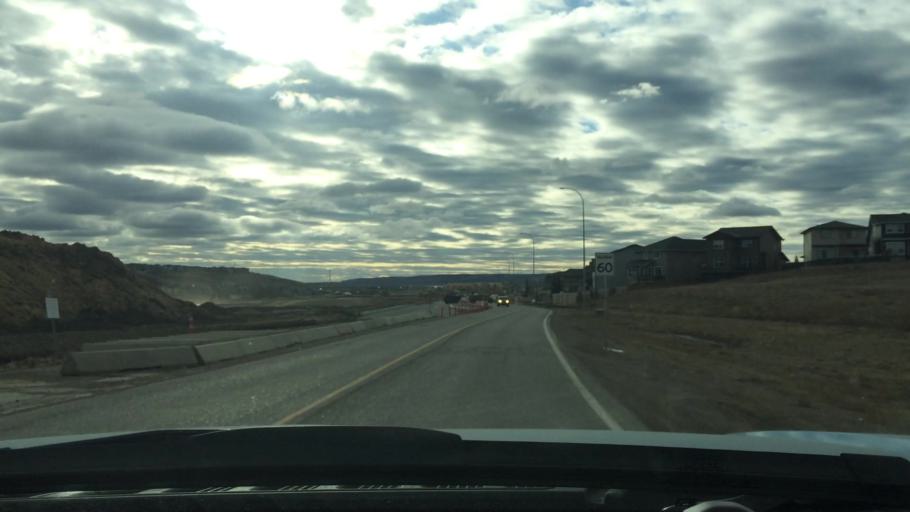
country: CA
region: Alberta
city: Calgary
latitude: 51.1830
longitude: -114.1350
